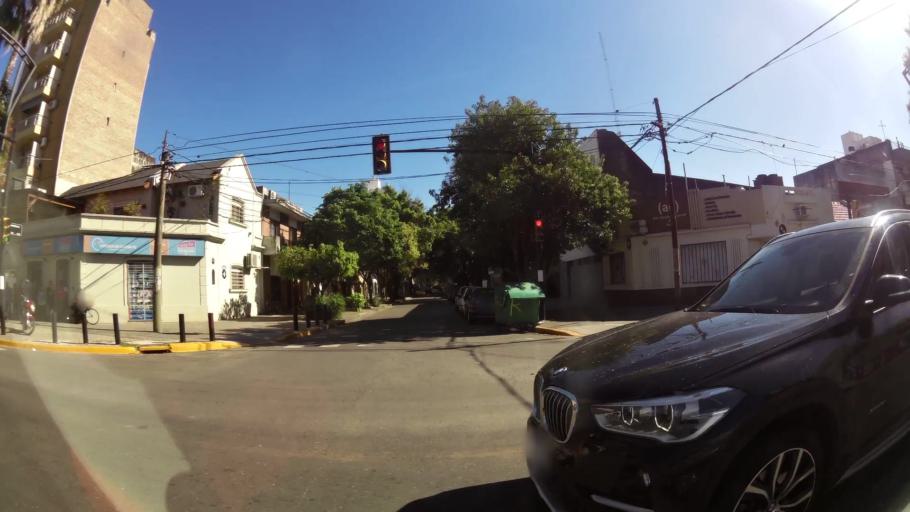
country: AR
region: Santa Fe
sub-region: Departamento de Rosario
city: Rosario
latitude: -32.9506
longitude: -60.6778
